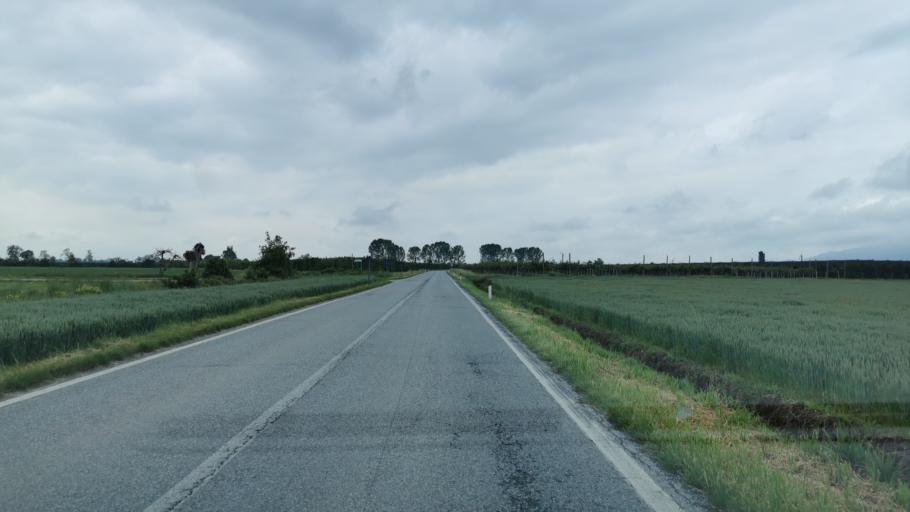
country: IT
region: Piedmont
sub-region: Provincia di Cuneo
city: Lagnasco
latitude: 44.6020
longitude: 7.5703
